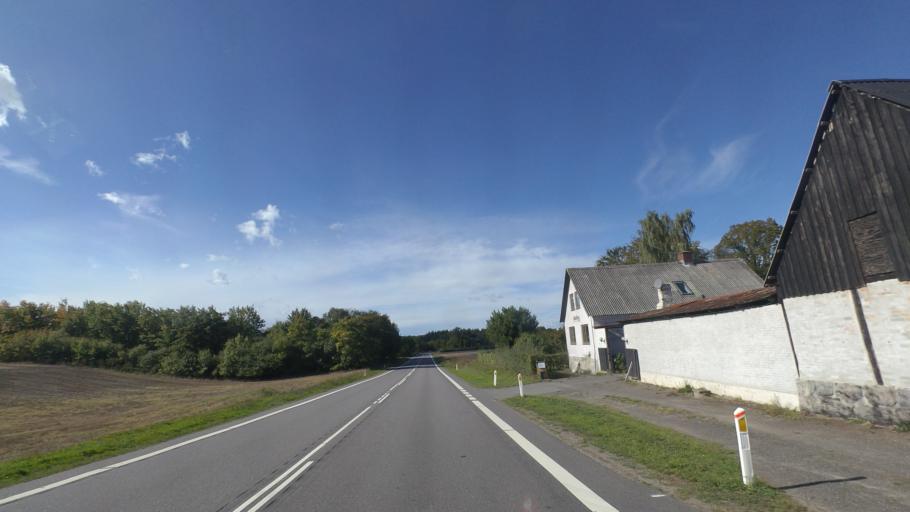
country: DK
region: Capital Region
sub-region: Bornholm Kommune
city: Ronne
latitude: 55.0791
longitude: 14.7622
